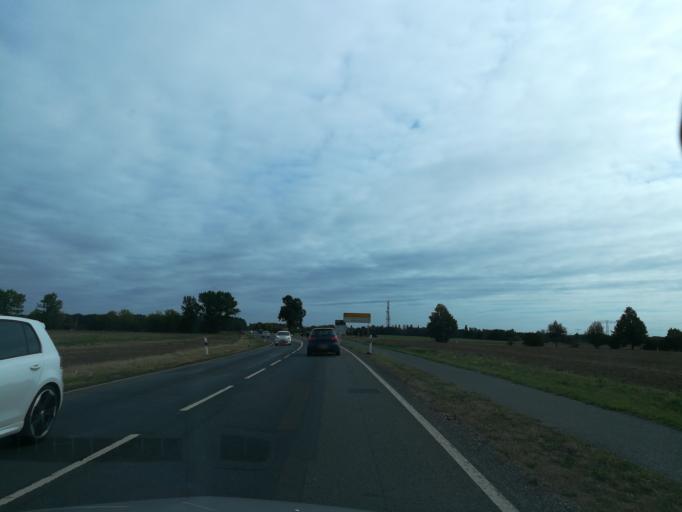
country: DE
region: Saxony-Anhalt
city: Ebendorf
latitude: 52.1735
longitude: 11.5908
